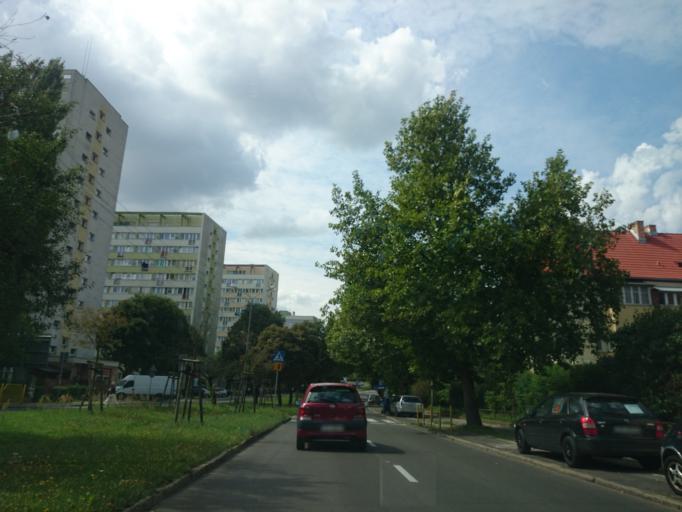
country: PL
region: West Pomeranian Voivodeship
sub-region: Szczecin
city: Szczecin
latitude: 53.4329
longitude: 14.5093
